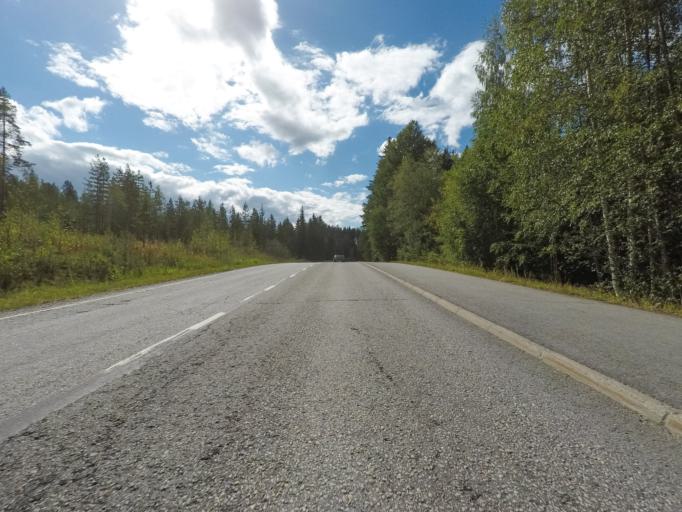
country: FI
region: Central Finland
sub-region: Jyvaeskylae
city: Toivakka
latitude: 62.0882
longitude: 26.0660
